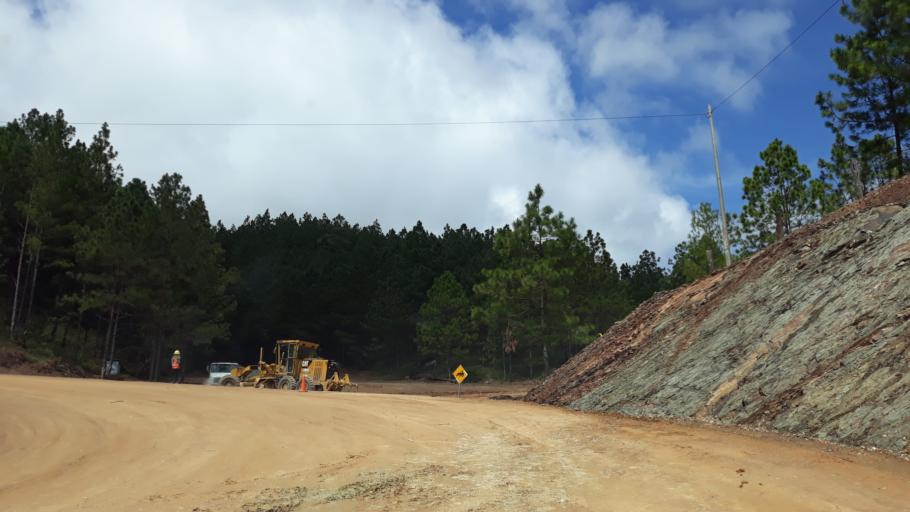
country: HN
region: El Paraiso
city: Santa Cruz
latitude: 13.7684
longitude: -86.6417
